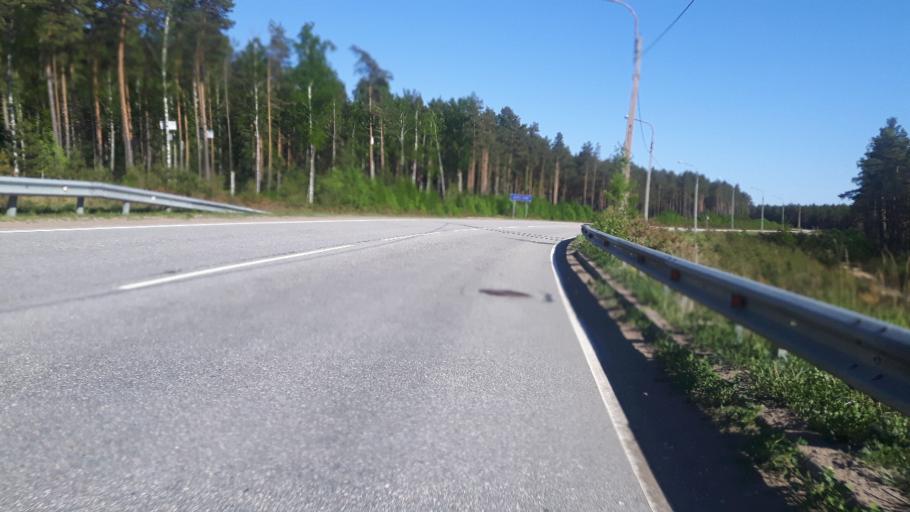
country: RU
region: Leningrad
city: Sosnovyy Bor
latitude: 60.1893
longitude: 29.0205
